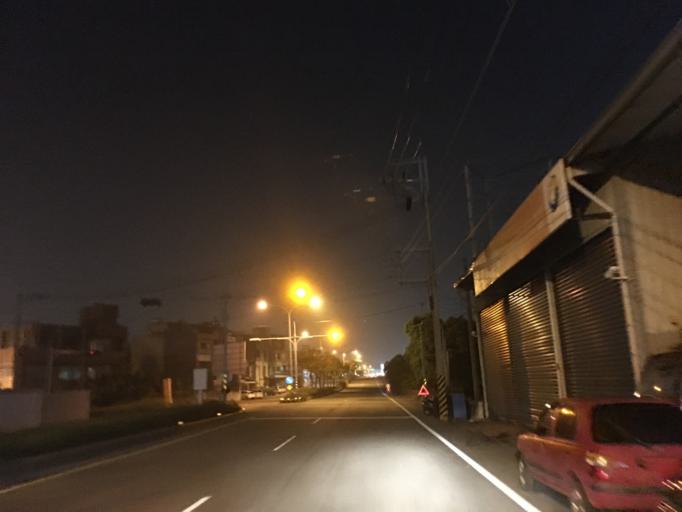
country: TW
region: Taiwan
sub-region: Hsinchu
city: Hsinchu
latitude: 24.6964
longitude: 120.8854
